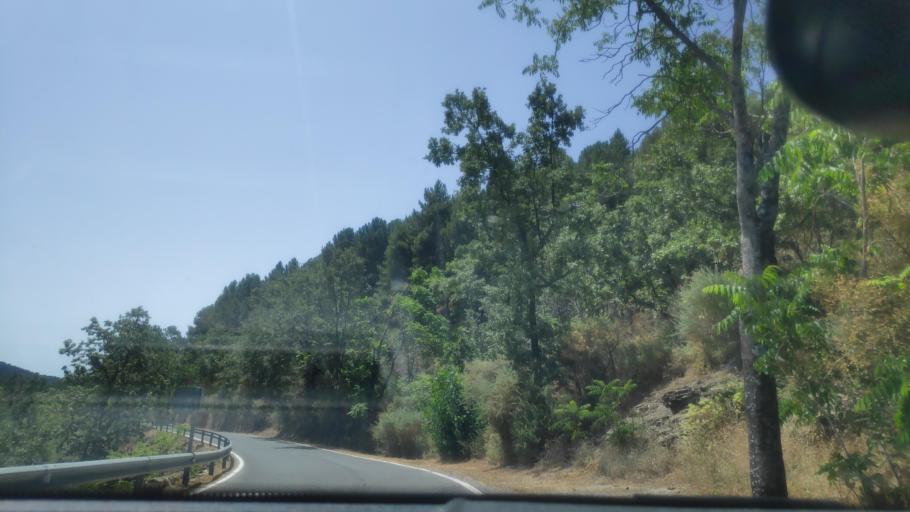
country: ES
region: Andalusia
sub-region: Provincia de Granada
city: Busquistar
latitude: 36.9648
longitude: -3.2816
